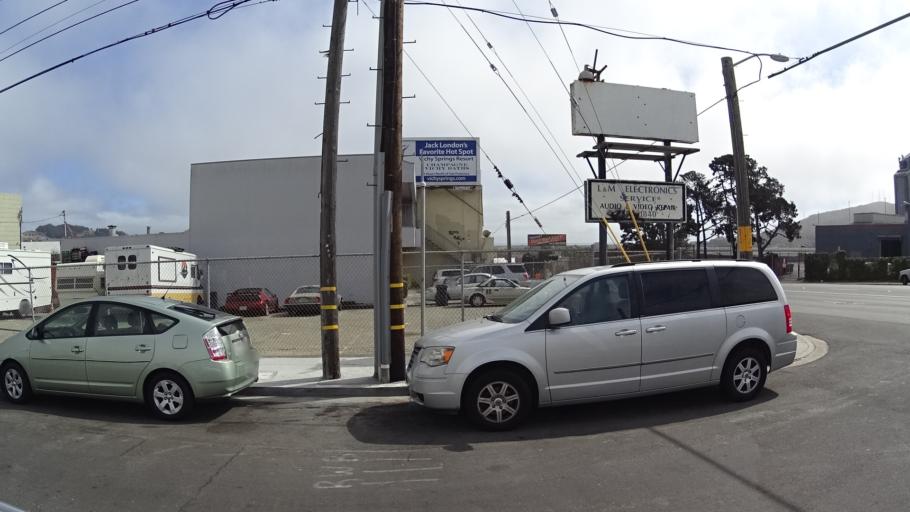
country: US
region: California
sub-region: San Mateo County
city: Brisbane
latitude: 37.7081
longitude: -122.4183
